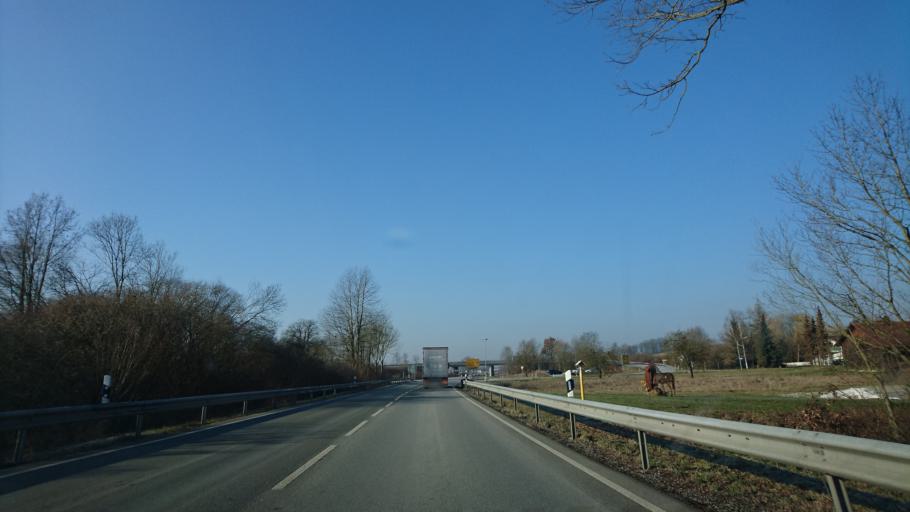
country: DE
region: Bavaria
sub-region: Lower Bavaria
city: Bad Griesbach
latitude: 48.4180
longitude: 13.1826
